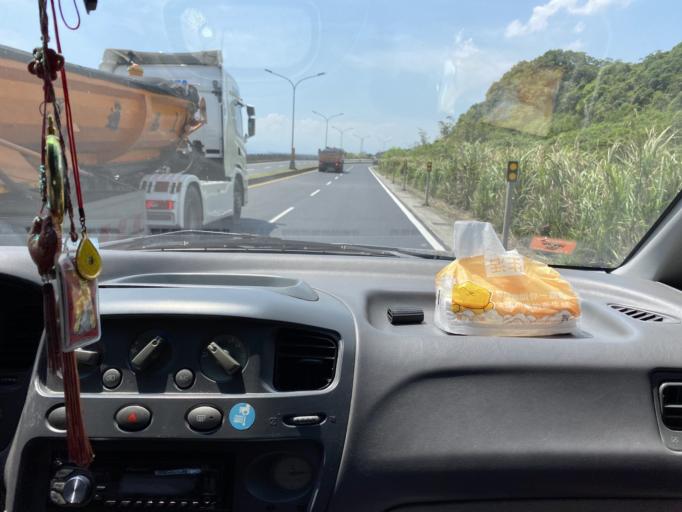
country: TW
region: Taiwan
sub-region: Yilan
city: Yilan
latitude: 24.8963
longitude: 121.8598
